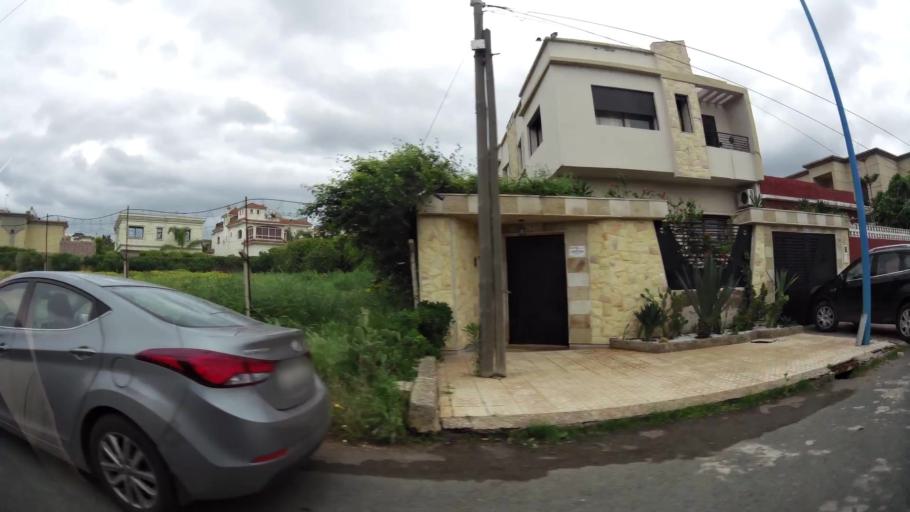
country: MA
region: Grand Casablanca
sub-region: Casablanca
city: Casablanca
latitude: 33.5497
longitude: -7.6341
